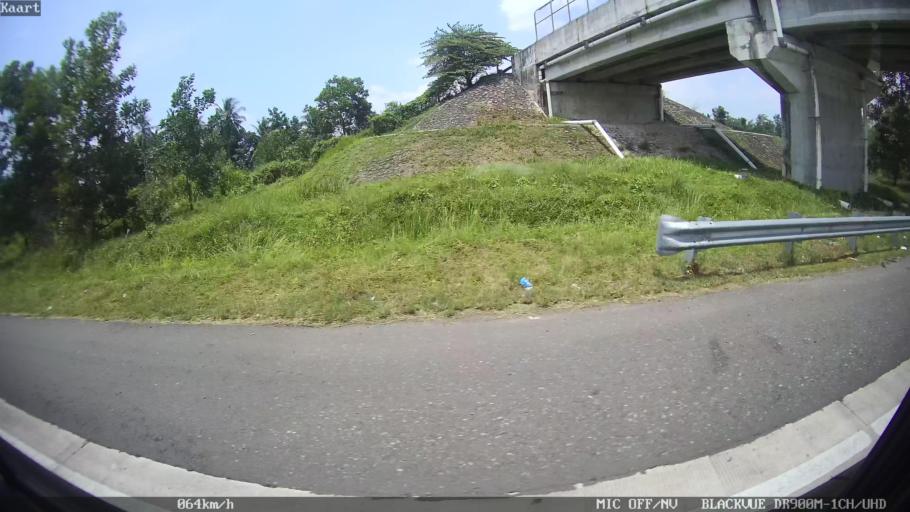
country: ID
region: Lampung
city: Natar
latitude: -5.2948
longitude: 105.2372
